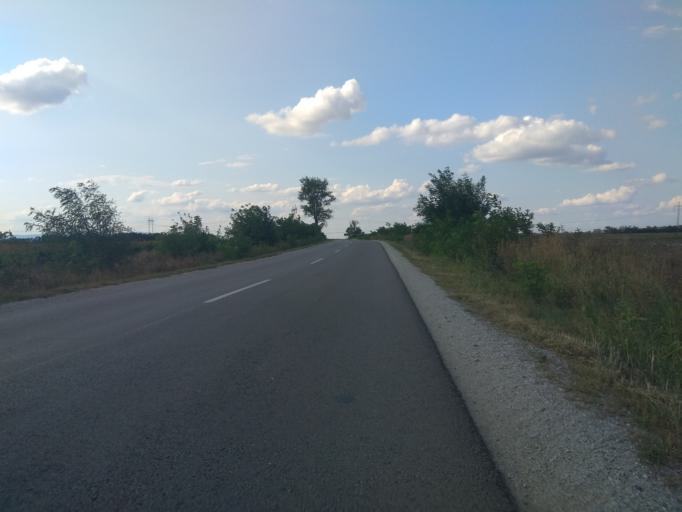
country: HU
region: Borsod-Abauj-Zemplen
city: Hejobaba
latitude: 47.9027
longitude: 20.8895
